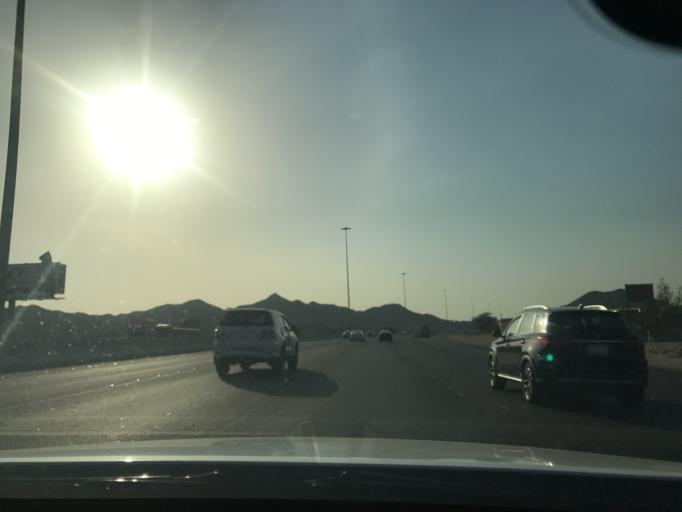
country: SA
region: Makkah
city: Jeddah
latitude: 21.3908
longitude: 39.4155
